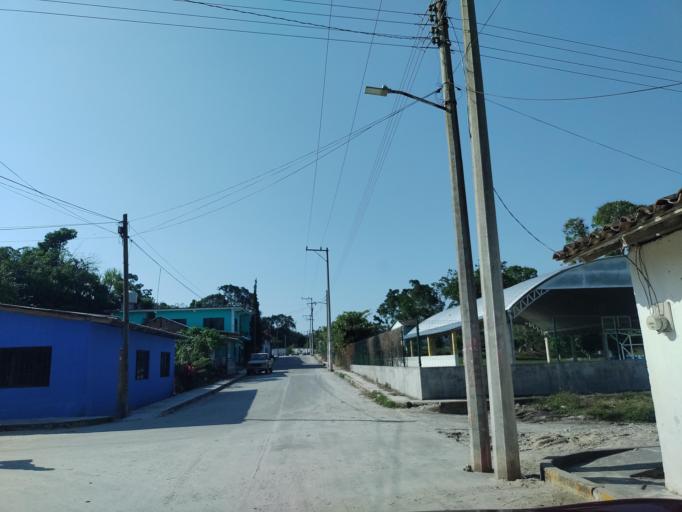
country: MX
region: Veracruz
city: Agua Dulce
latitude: 20.2571
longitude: -97.2528
